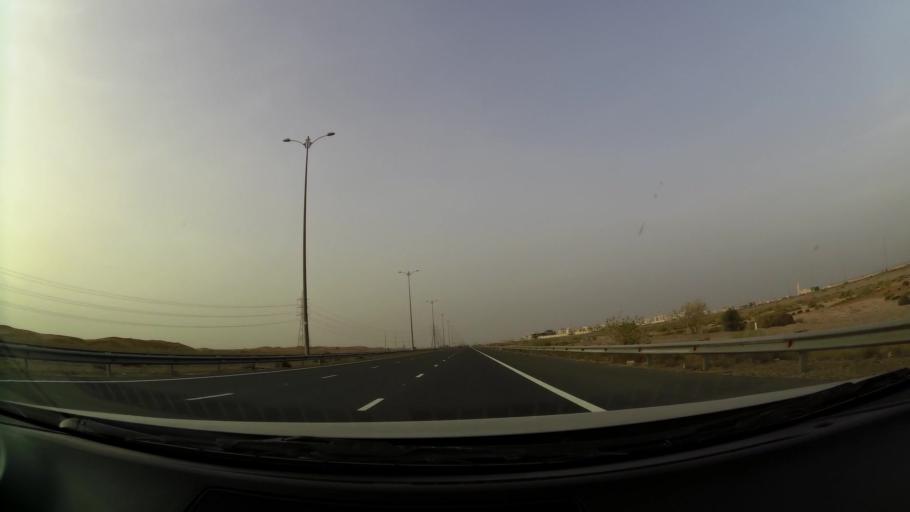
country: OM
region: Al Buraimi
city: Al Buraymi
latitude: 24.3420
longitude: 55.7747
